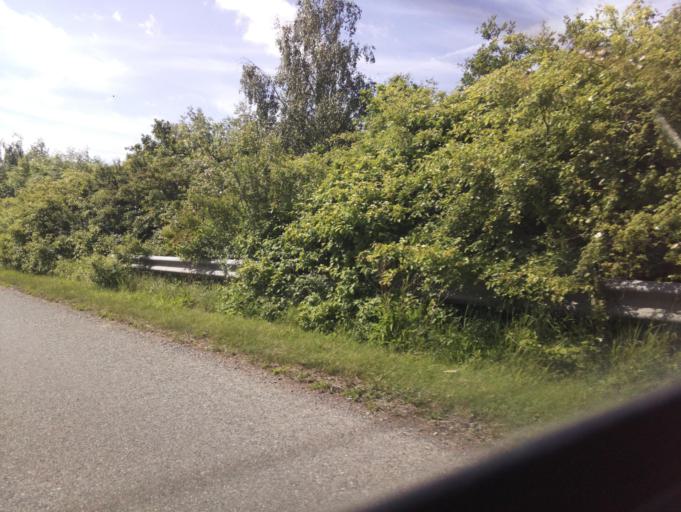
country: GB
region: England
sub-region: Lincolnshire
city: Skellingthorpe
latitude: 53.1676
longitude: -0.6433
